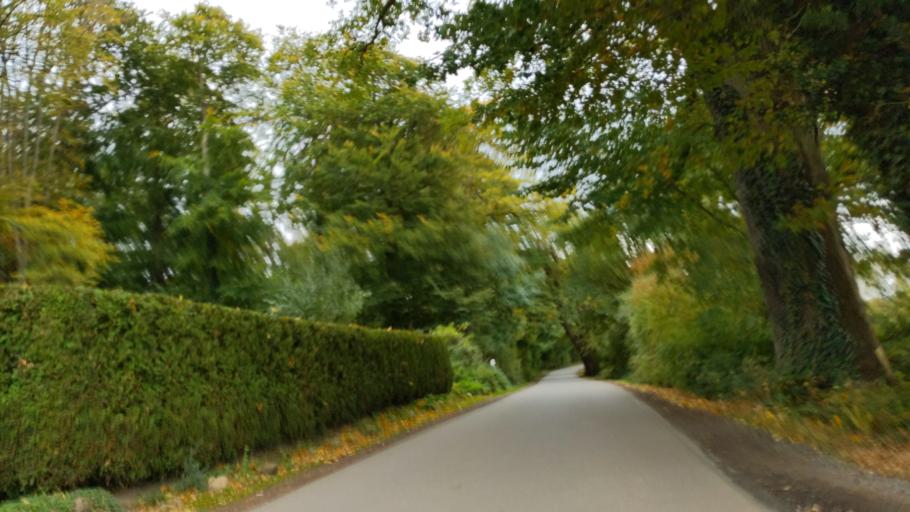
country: DE
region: Schleswig-Holstein
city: Neustadt in Holstein
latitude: 54.1337
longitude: 10.7832
